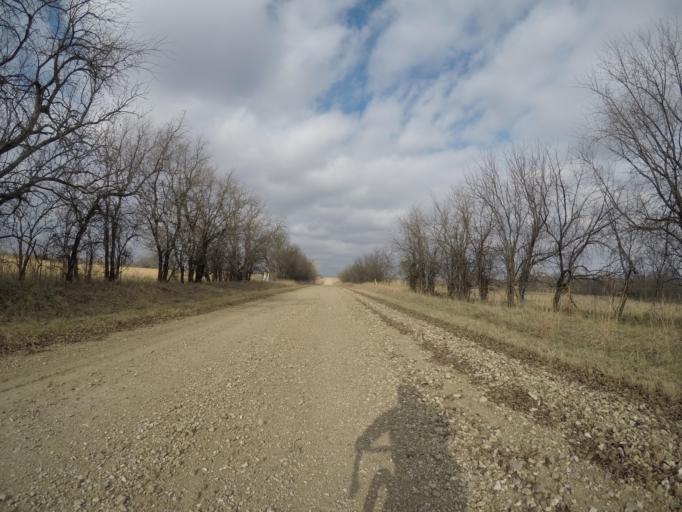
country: US
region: Kansas
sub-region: Morris County
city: Council Grove
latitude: 38.7852
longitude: -96.3527
